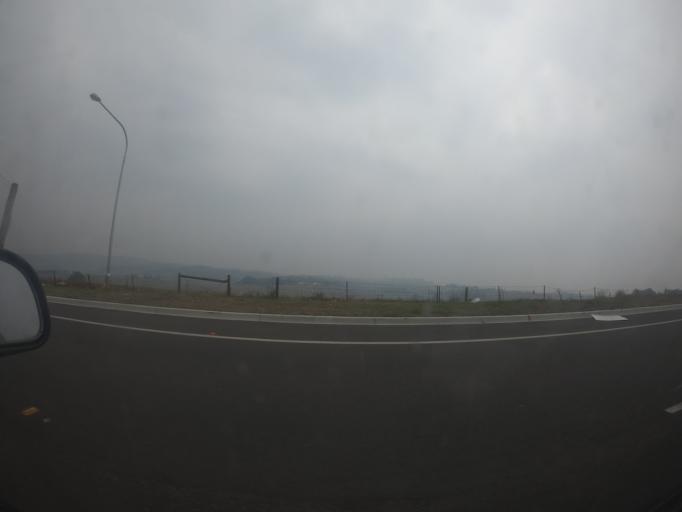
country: AU
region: New South Wales
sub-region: Shellharbour
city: Croom
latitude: -34.5988
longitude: 150.8462
